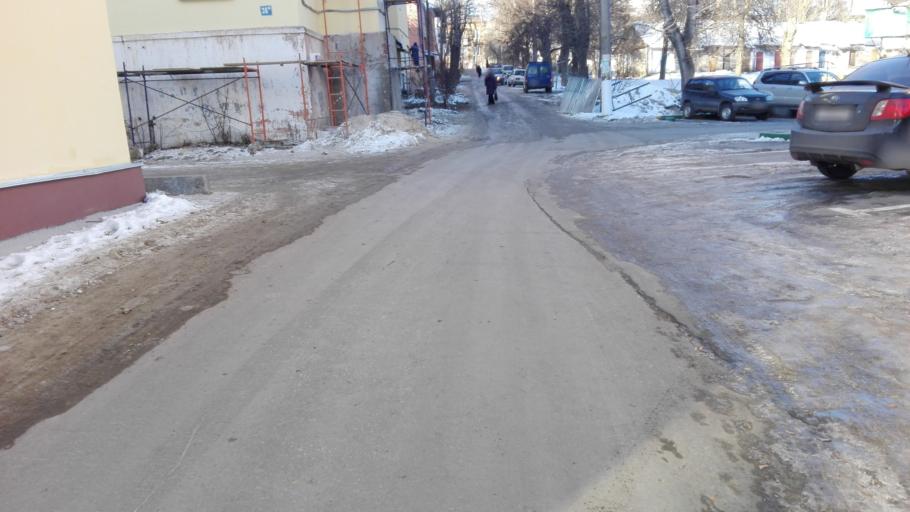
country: RU
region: Tula
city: Kosaya Gora
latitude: 54.1161
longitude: 37.5414
